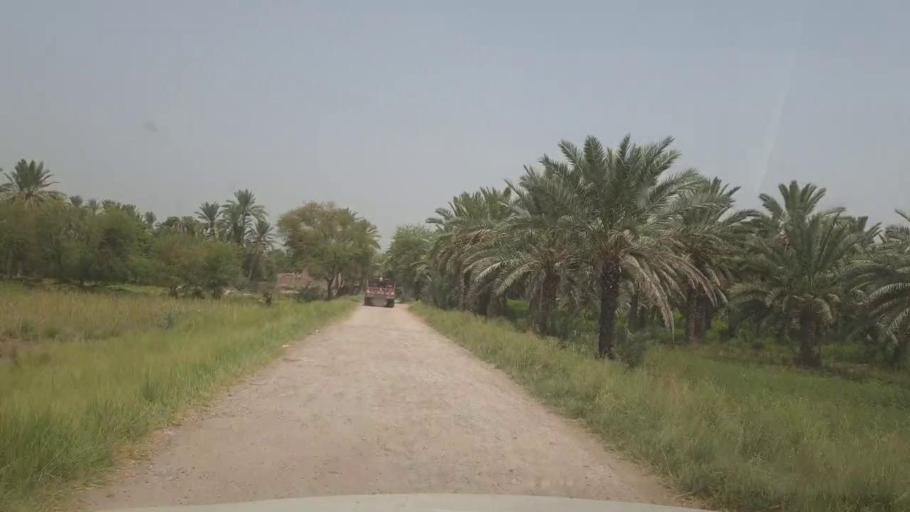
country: PK
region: Sindh
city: Kot Diji
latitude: 27.3497
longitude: 68.7048
